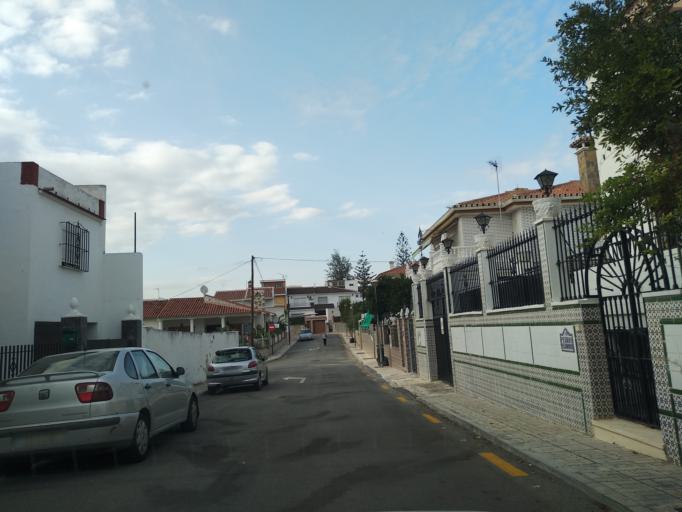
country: ES
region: Andalusia
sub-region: Provincia de Malaga
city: Malaga
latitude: 36.7373
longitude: -4.4780
